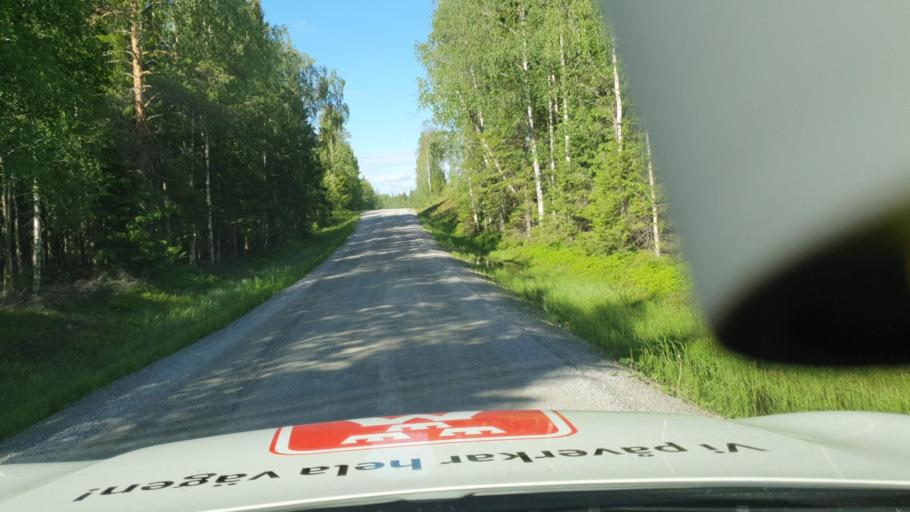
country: SE
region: Vaesterbotten
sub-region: Vannas Kommun
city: Vaennaes
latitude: 63.8010
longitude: 19.6344
